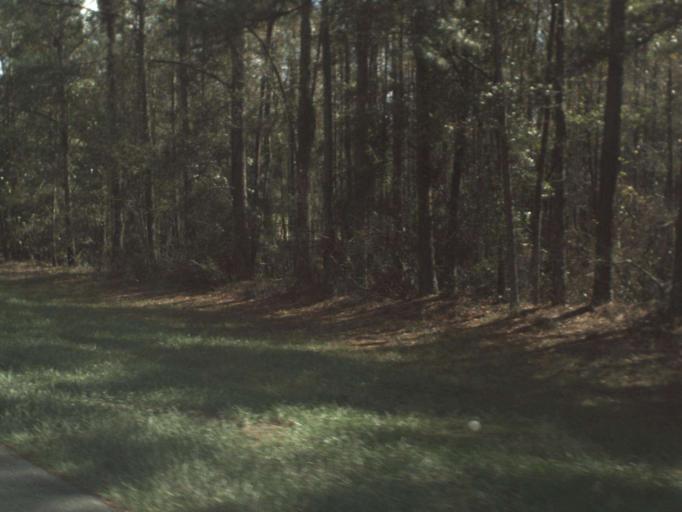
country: US
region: Florida
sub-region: Jackson County
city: Marianna
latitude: 30.7413
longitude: -85.1490
